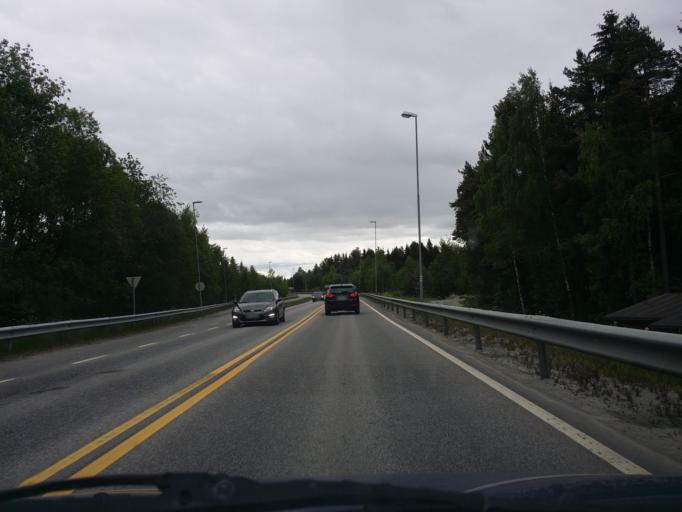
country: NO
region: Hedmark
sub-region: Ringsaker
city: Moelv
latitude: 60.9222
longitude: 10.6932
